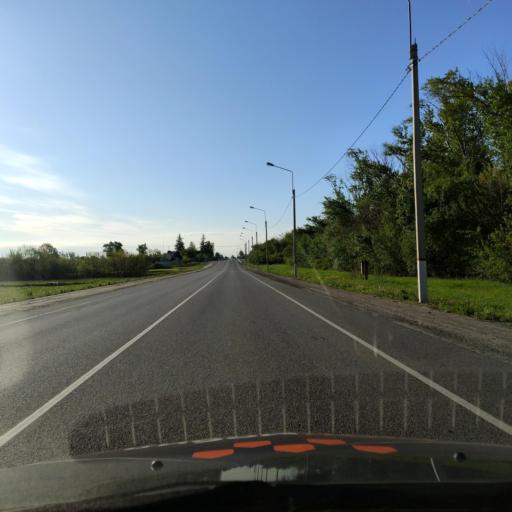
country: RU
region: Lipetsk
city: Yelets
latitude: 52.5591
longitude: 38.6896
